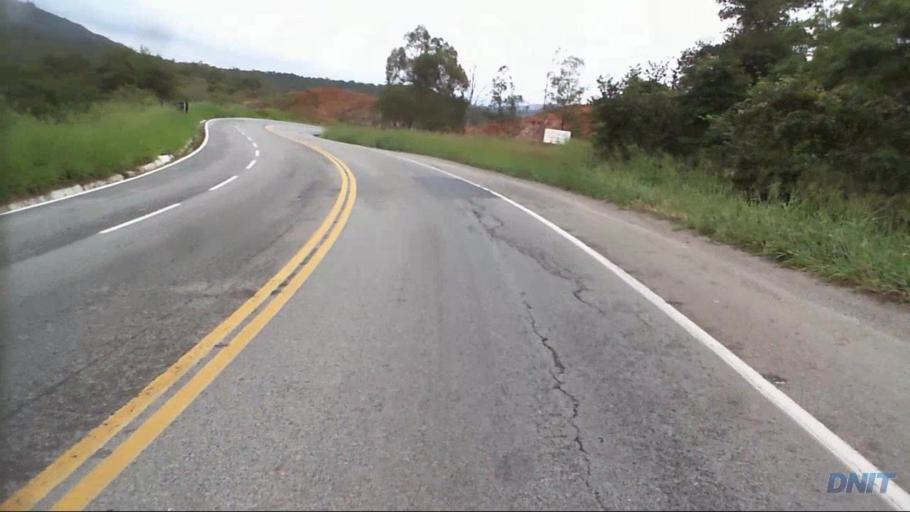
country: BR
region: Minas Gerais
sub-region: Joao Monlevade
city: Joao Monlevade
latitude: -19.8432
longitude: -43.3131
